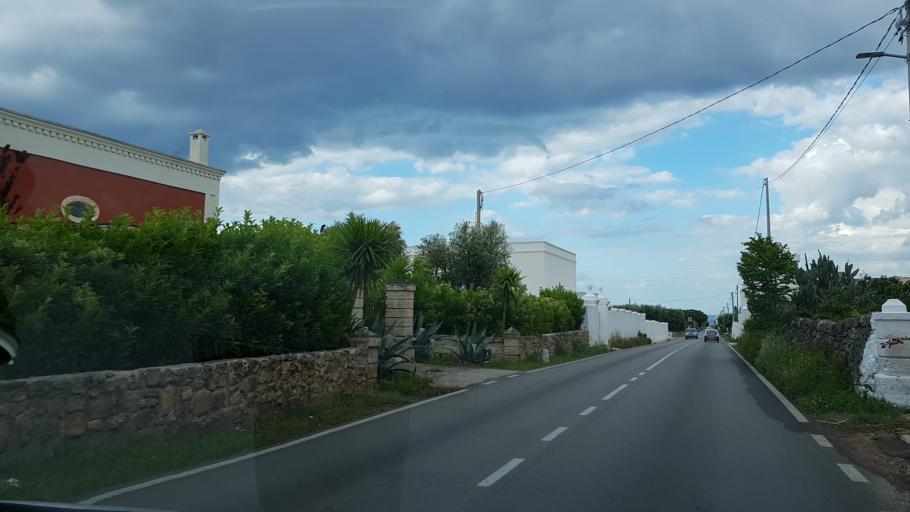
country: IT
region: Apulia
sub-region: Provincia di Brindisi
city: Fasano
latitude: 40.8442
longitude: 17.3783
